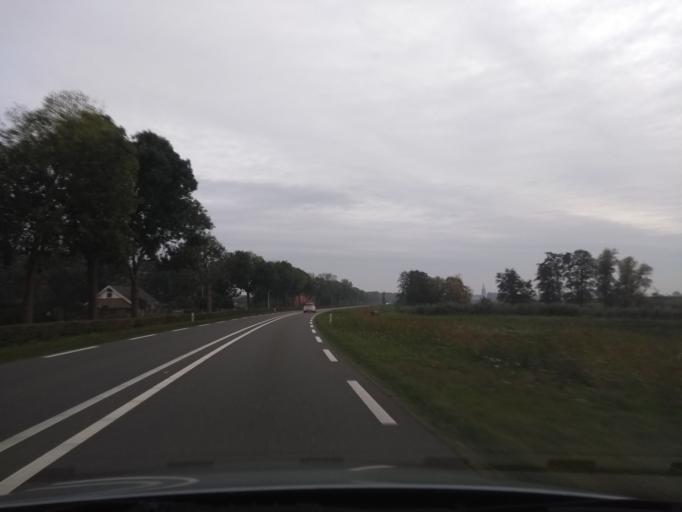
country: NL
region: Overijssel
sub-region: Gemeente Zwartewaterland
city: Hasselt
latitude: 52.6047
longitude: 6.0985
